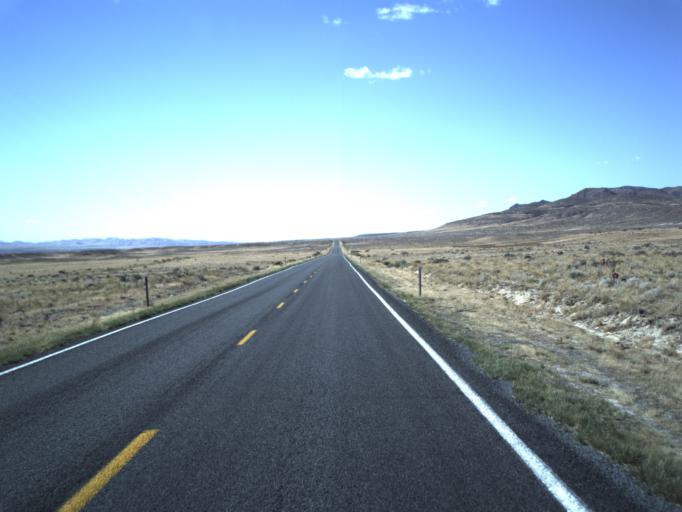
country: US
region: Utah
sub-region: Millard County
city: Fillmore
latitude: 38.9016
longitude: -112.8216
